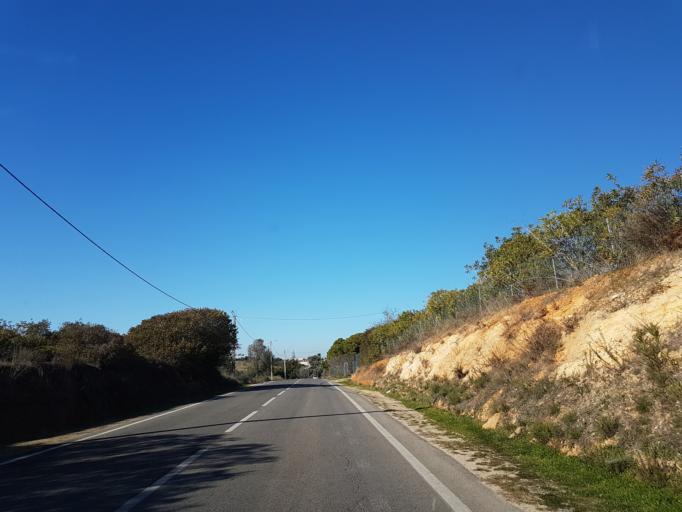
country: PT
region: Faro
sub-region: Lagoa
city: Carvoeiro
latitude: 37.1116
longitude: -8.4482
